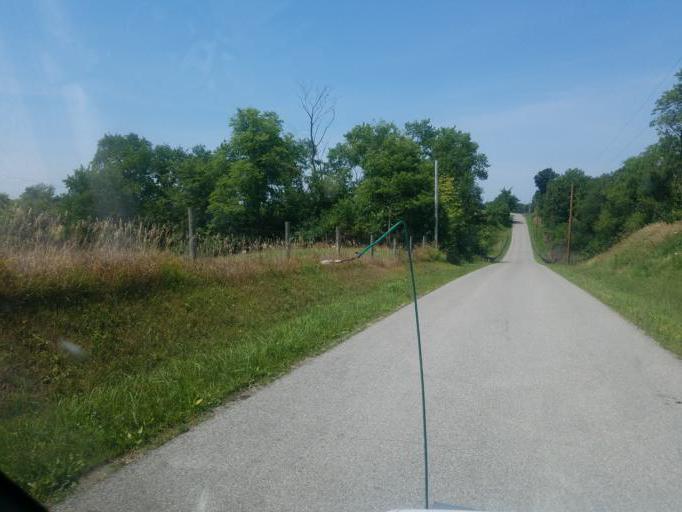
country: US
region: Ohio
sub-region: Logan County
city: De Graff
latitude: 40.2929
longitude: -83.8330
